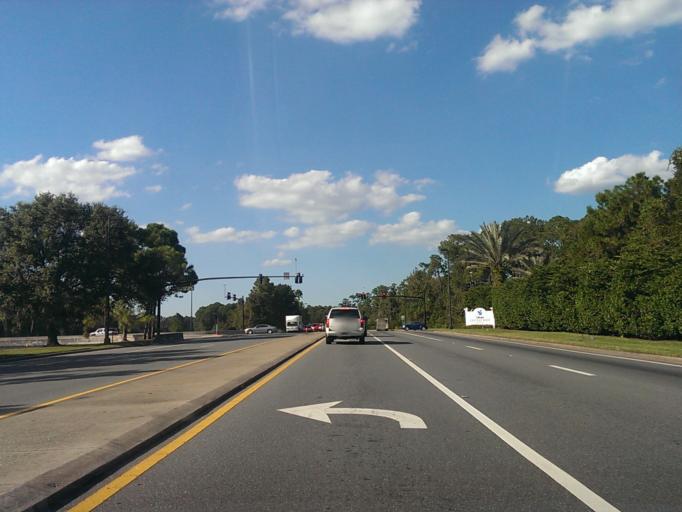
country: US
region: Florida
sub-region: Osceola County
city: Celebration
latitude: 28.3756
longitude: -81.5374
